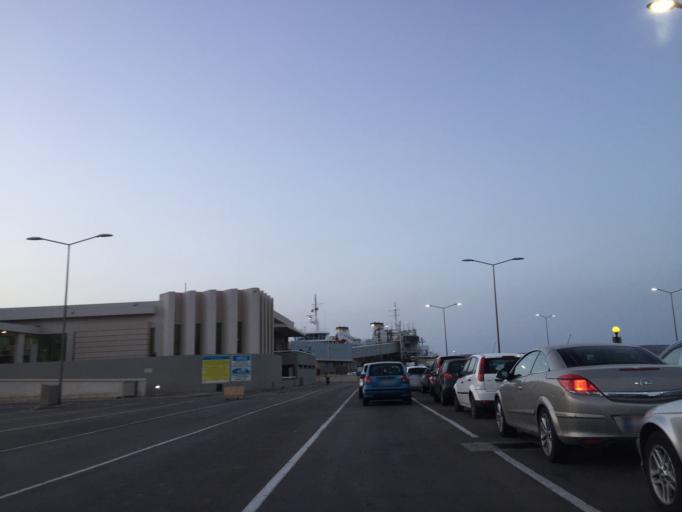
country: MT
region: Il-Mellieha
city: Mellieha
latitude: 35.9876
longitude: 14.3292
